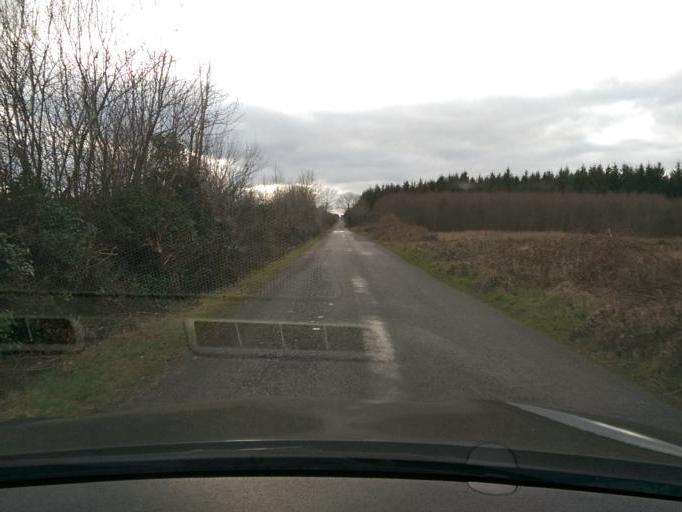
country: IE
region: Leinster
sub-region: Uibh Fhaili
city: Ferbane
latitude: 53.3300
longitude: -7.8557
